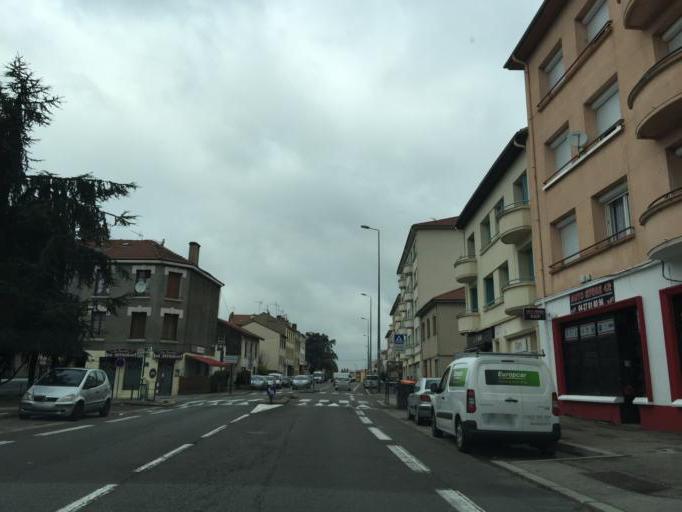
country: FR
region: Rhone-Alpes
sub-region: Departement de la Loire
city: Saint-Etienne
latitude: 45.4484
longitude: 4.4037
